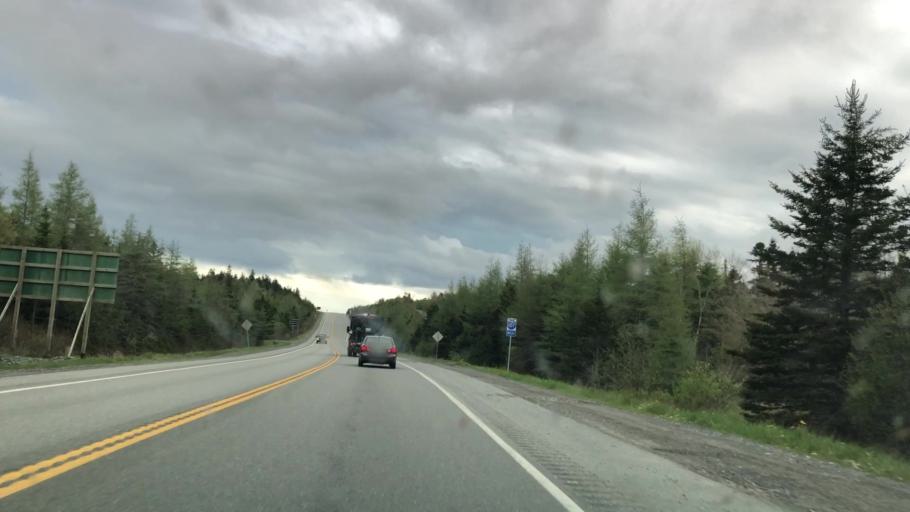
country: CA
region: Nova Scotia
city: Cole Harbour
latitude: 44.7809
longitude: -63.1777
